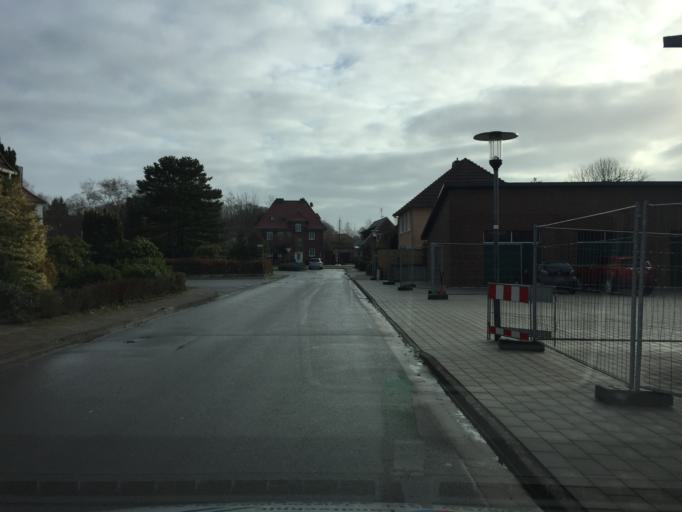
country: DE
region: Lower Saxony
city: Sulingen
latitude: 52.6797
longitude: 8.8103
